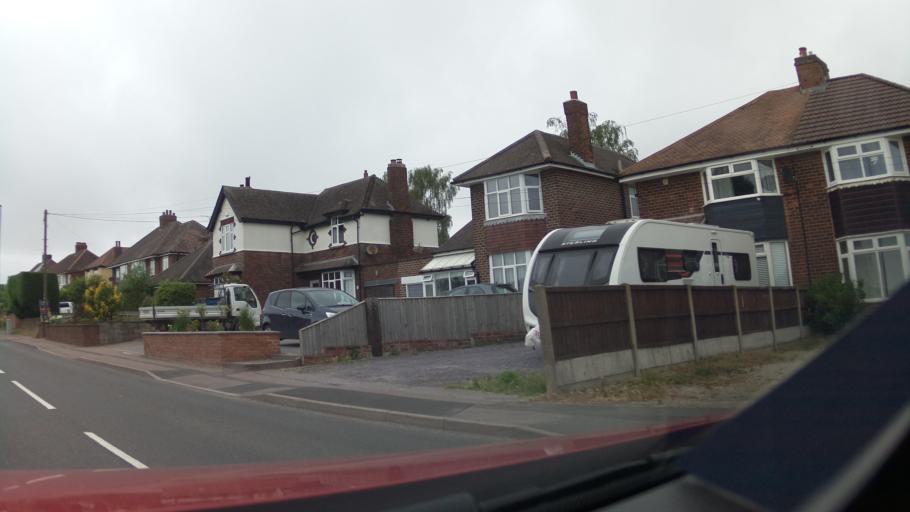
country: GB
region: England
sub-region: Staffordshire
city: Burton upon Trent
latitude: 52.7820
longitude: -1.6095
